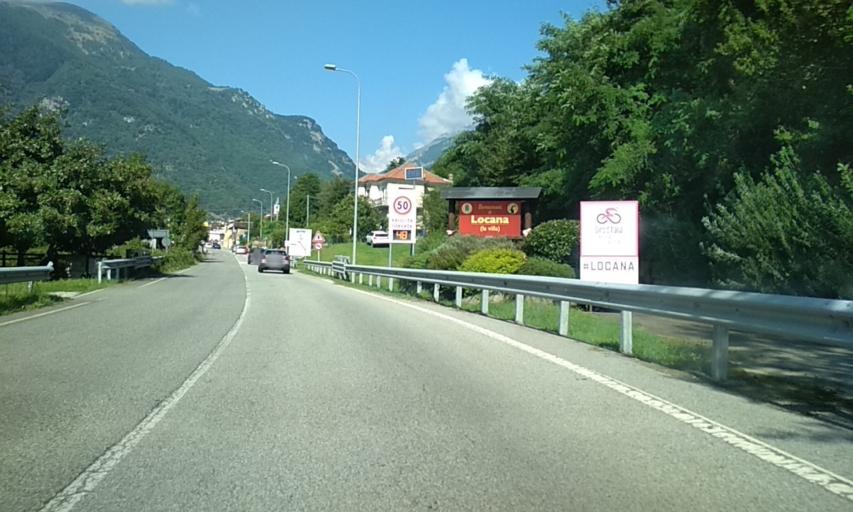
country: IT
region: Piedmont
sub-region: Provincia di Torino
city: Locana
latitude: 45.4161
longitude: 7.4672
